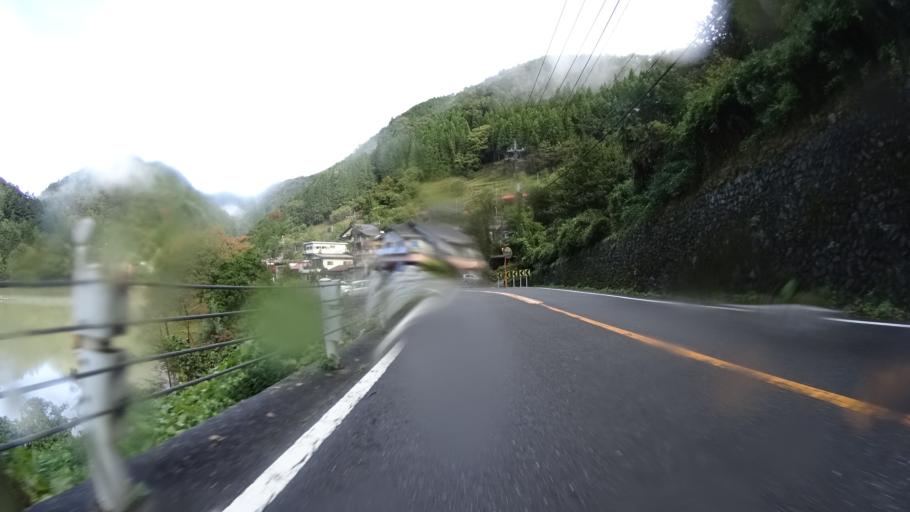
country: JP
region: Yamanashi
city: Otsuki
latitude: 35.7772
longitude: 138.9907
